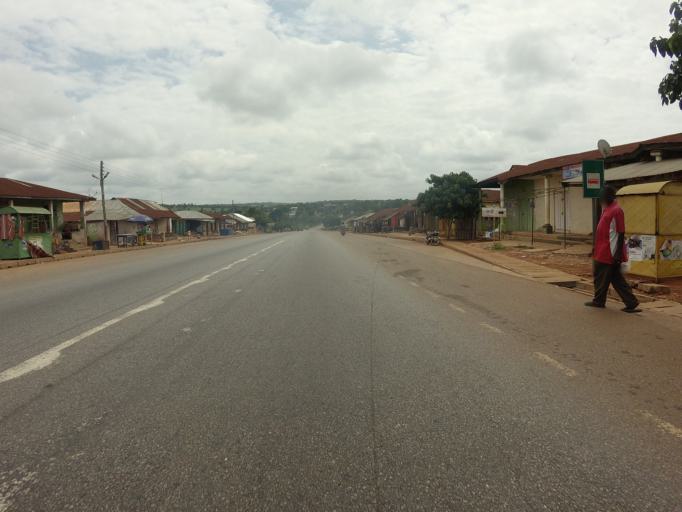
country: GH
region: Brong-Ahafo
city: Techiman
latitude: 7.4586
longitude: -1.9718
